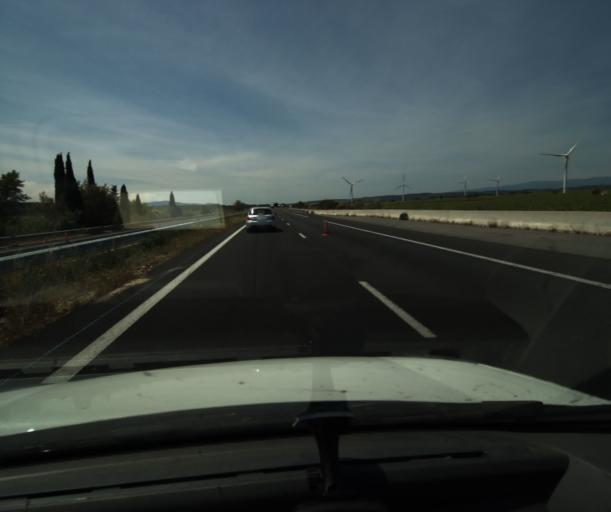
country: FR
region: Languedoc-Roussillon
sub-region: Departement de l'Aude
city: Ornaisons
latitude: 43.1673
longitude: 2.8235
